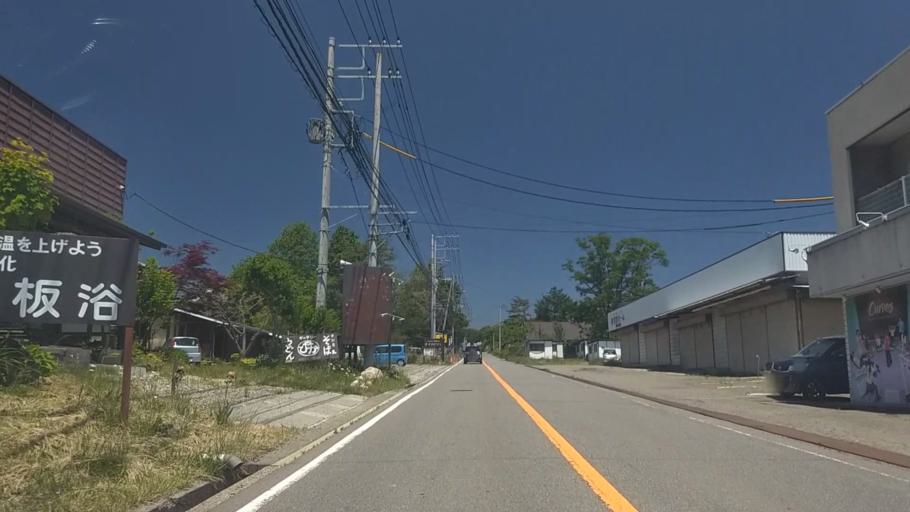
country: JP
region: Yamanashi
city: Nirasaki
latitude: 35.8482
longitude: 138.4325
